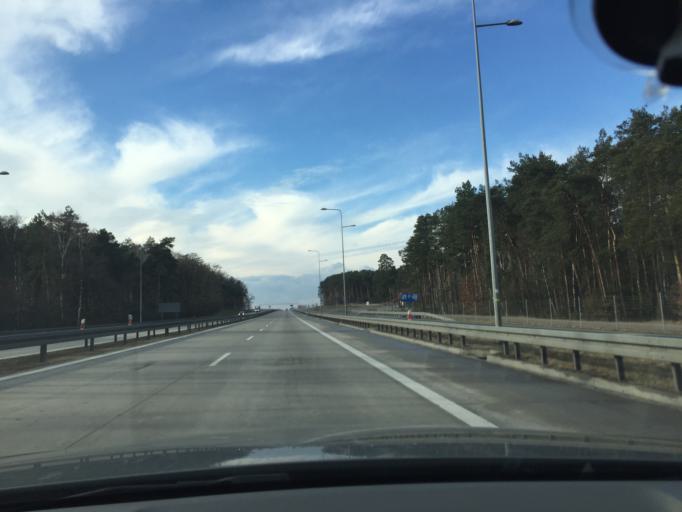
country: PL
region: Lodz Voivodeship
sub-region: Powiat piotrkowski
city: Wolborz
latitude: 51.4898
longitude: 19.8262
